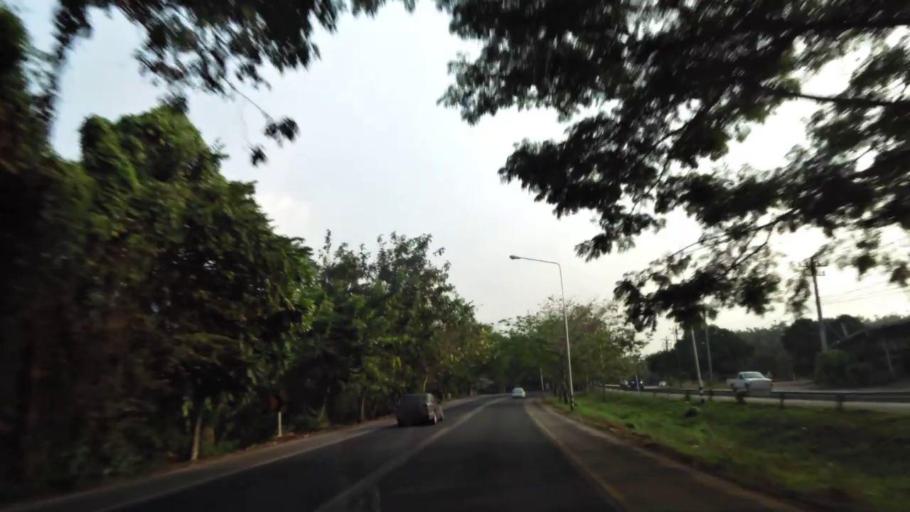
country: TH
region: Chanthaburi
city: Chanthaburi
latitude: 12.5717
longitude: 102.1625
